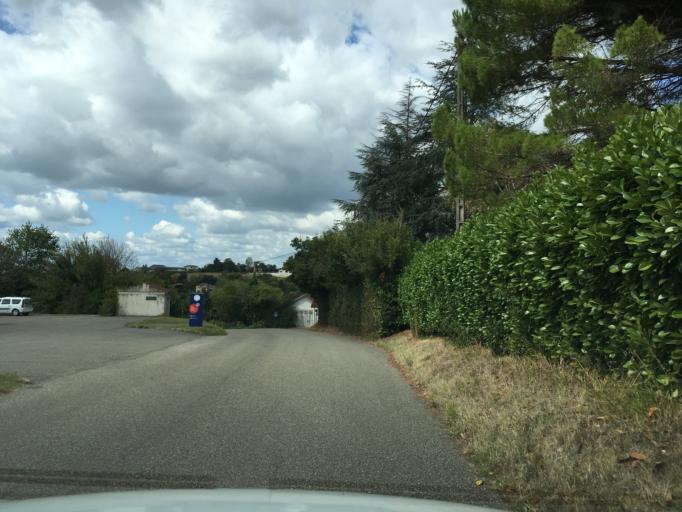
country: FR
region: Aquitaine
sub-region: Departement du Lot-et-Garonne
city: Agen
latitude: 44.2195
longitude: 0.6344
